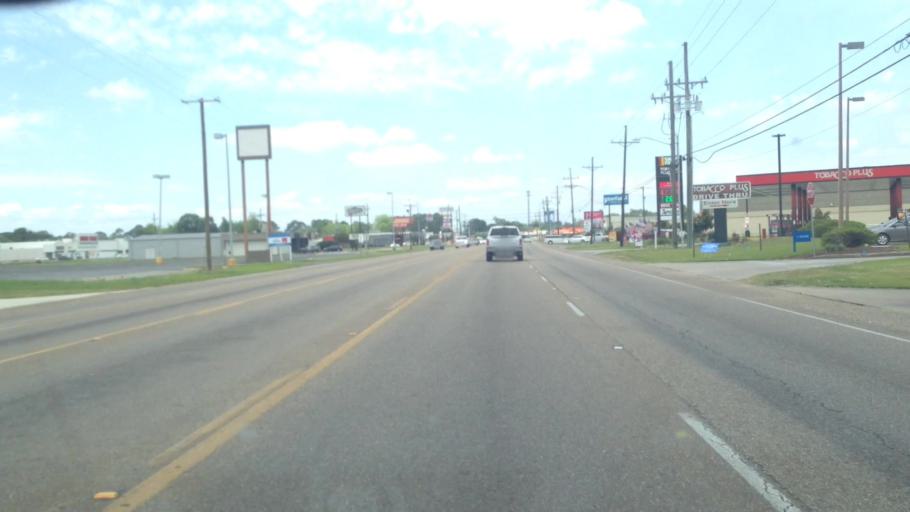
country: US
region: Louisiana
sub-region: Iberia Parish
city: New Iberia
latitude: 29.9861
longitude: -91.8212
